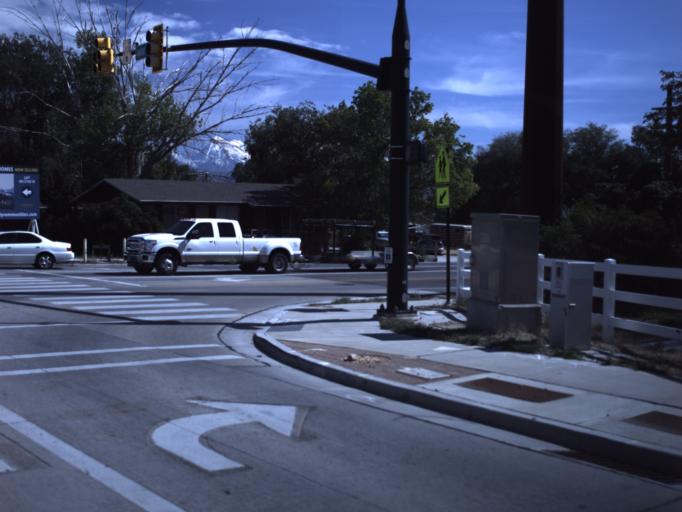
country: US
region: Utah
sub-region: Salt Lake County
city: South Jordan Heights
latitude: 40.5441
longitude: -111.9581
